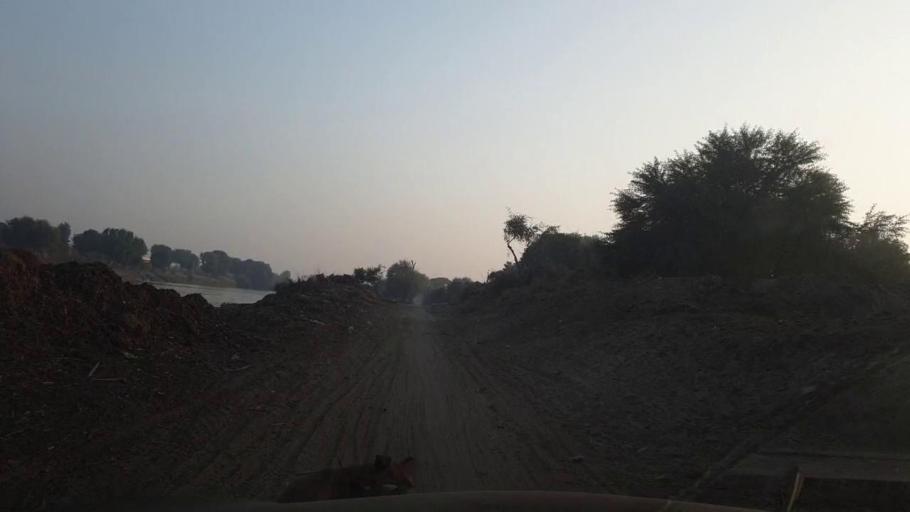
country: PK
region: Sindh
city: Ubauro
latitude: 28.3107
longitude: 69.7898
